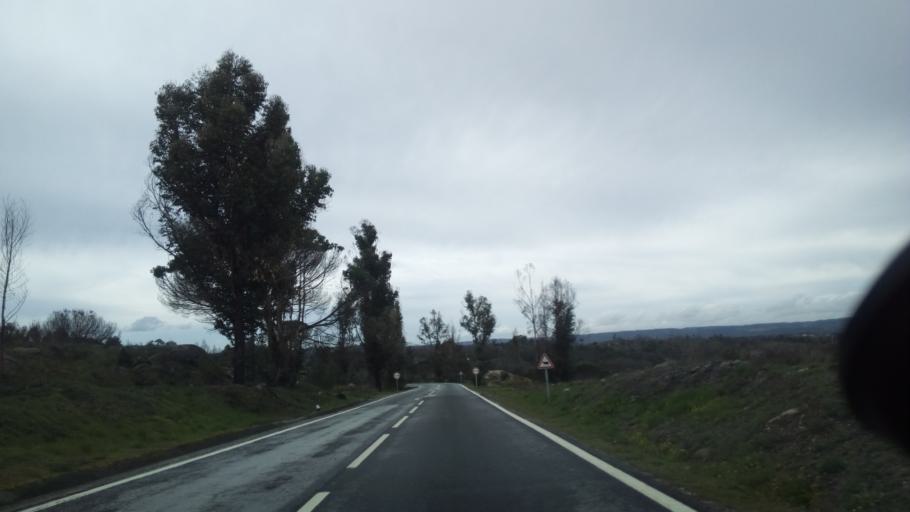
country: PT
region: Guarda
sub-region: Fornos de Algodres
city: Fornos de Algodres
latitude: 40.5236
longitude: -7.6018
